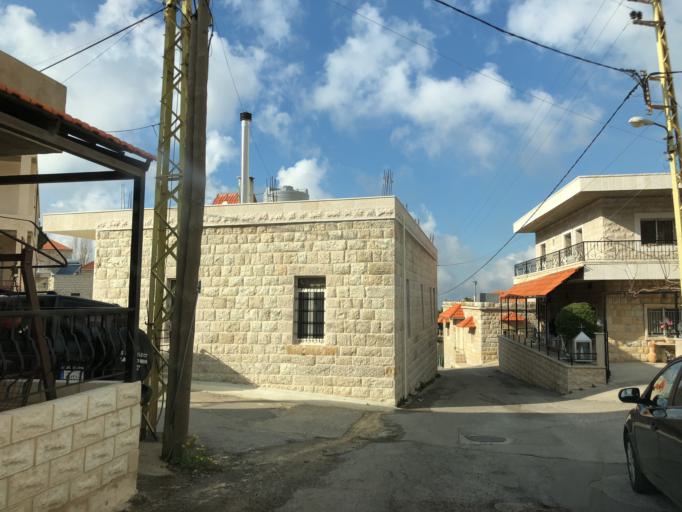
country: LB
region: Liban-Nord
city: Amioun
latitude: 34.2030
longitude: 35.8422
